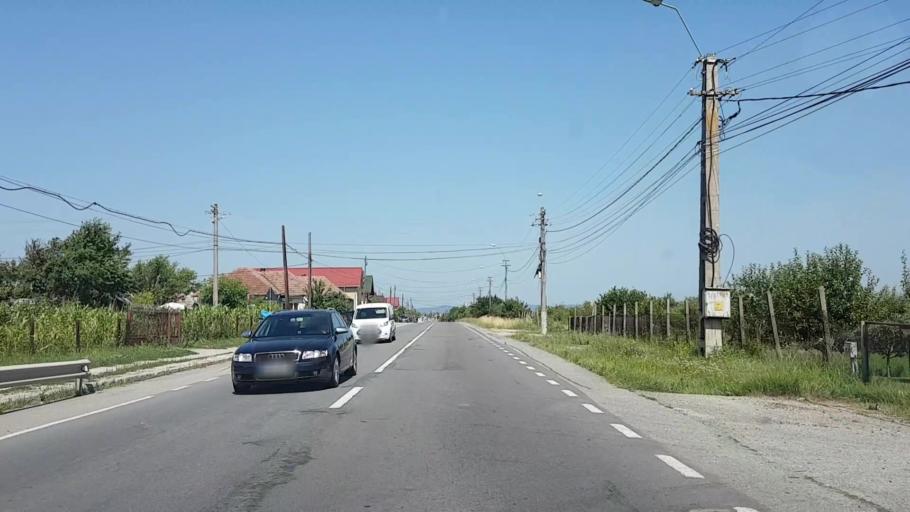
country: RO
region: Cluj
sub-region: Comuna Cusdrioara
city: Cusdrioara
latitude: 47.1723
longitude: 23.9287
